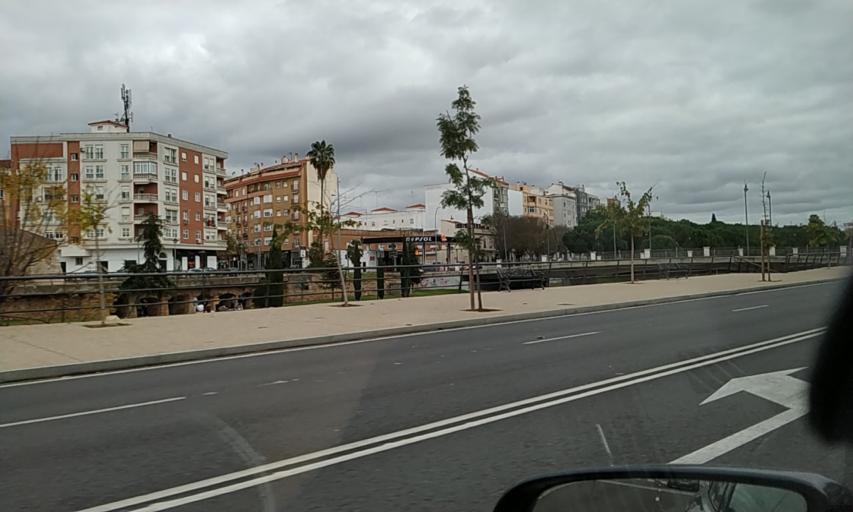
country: ES
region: Extremadura
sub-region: Provincia de Badajoz
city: Badajoz
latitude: 38.8793
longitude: -6.9636
